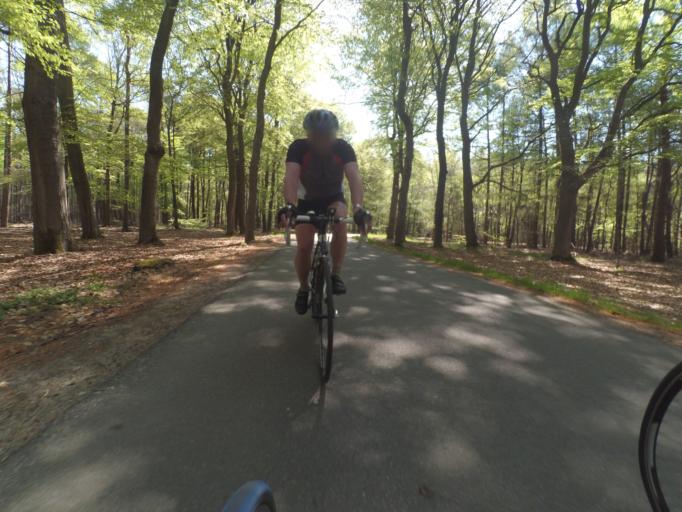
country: NL
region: Gelderland
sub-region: Gemeente Apeldoorn
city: Uddel
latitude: 52.2827
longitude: 5.7490
